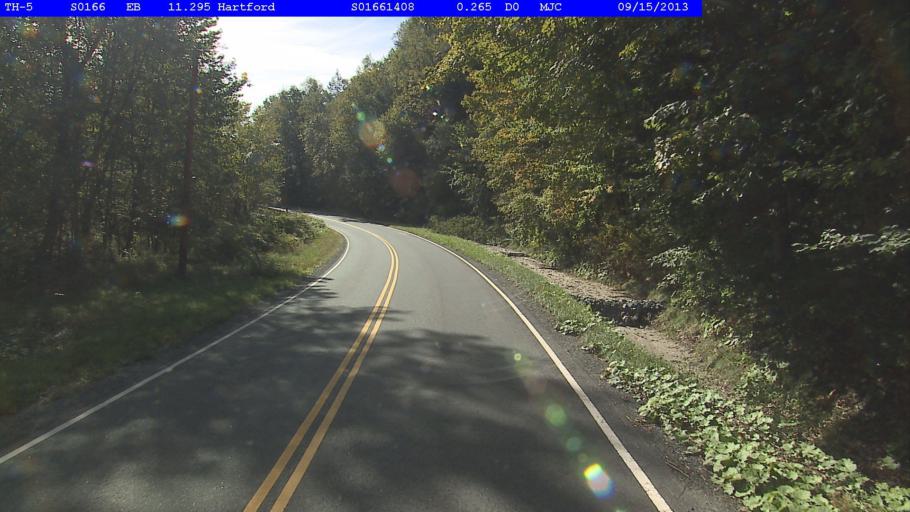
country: US
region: Vermont
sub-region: Windsor County
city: Wilder
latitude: 43.7193
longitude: -72.4226
